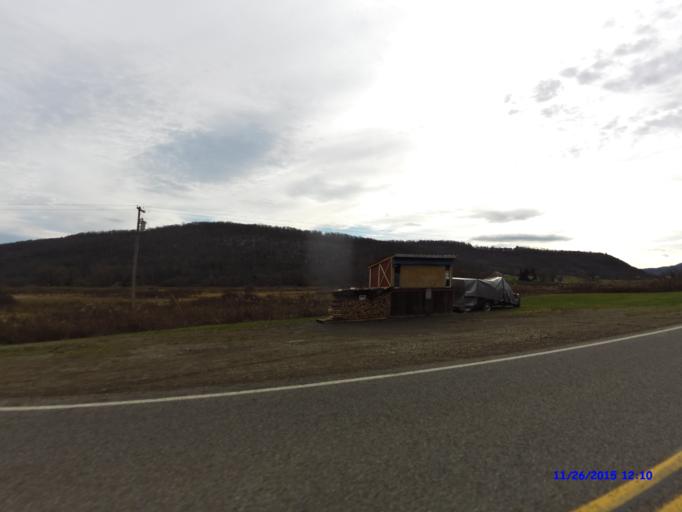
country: US
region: New York
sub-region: Cattaraugus County
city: Allegany
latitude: 42.1908
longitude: -78.4922
